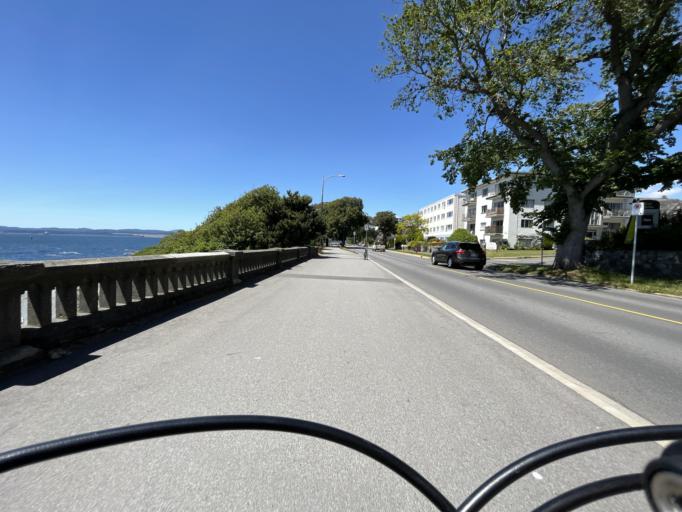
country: CA
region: British Columbia
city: Victoria
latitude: 48.4092
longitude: -123.3719
